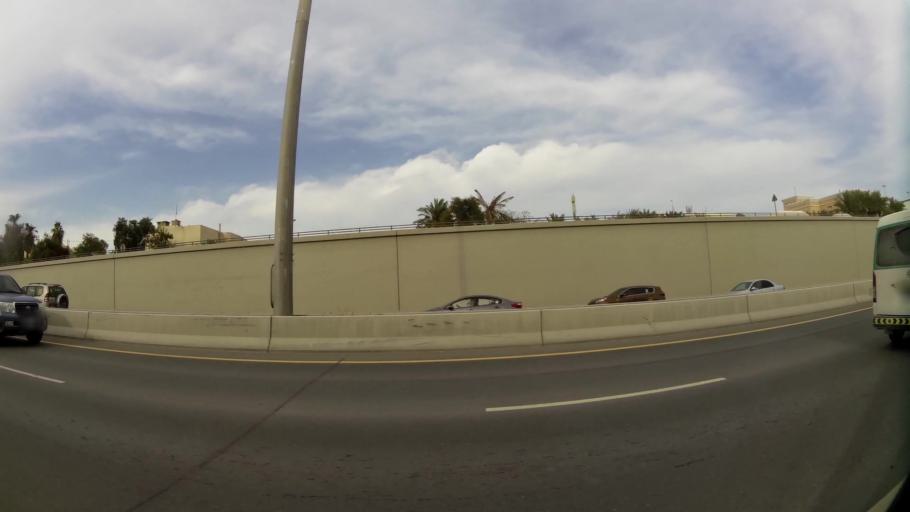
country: QA
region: Baladiyat ad Dawhah
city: Doha
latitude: 25.2773
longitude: 51.4879
